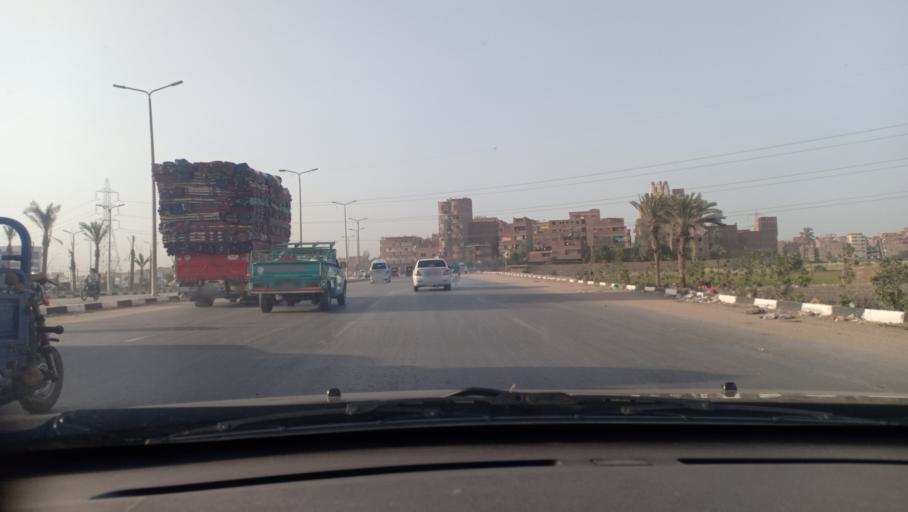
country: EG
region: Muhafazat al Qalyubiyah
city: Qalyub
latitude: 30.1391
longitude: 31.2643
